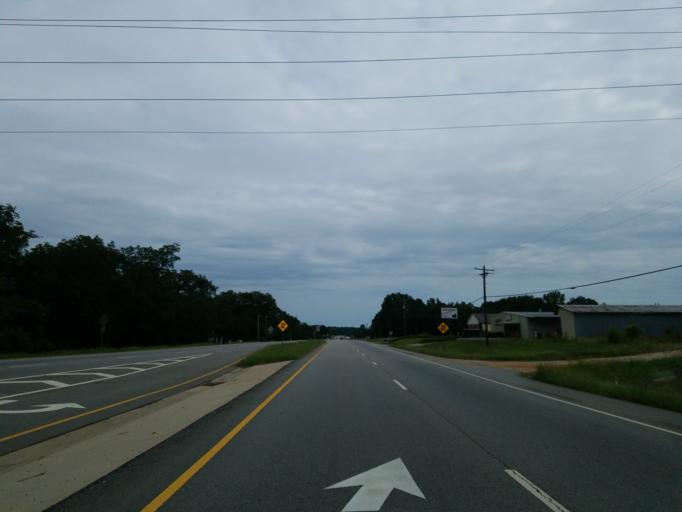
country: US
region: Georgia
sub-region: Lamar County
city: Barnesville
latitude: 33.0363
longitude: -84.1524
